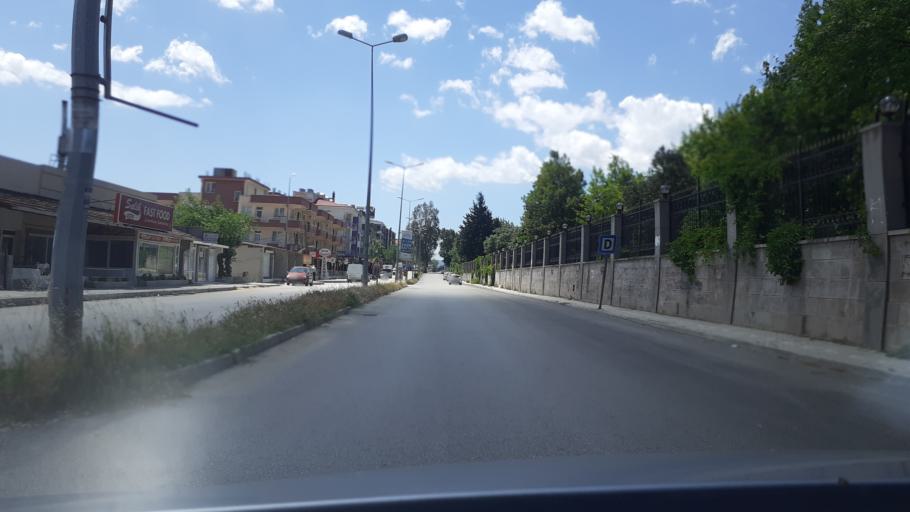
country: TR
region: Hatay
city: Anayazi
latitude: 36.3312
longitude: 36.1994
